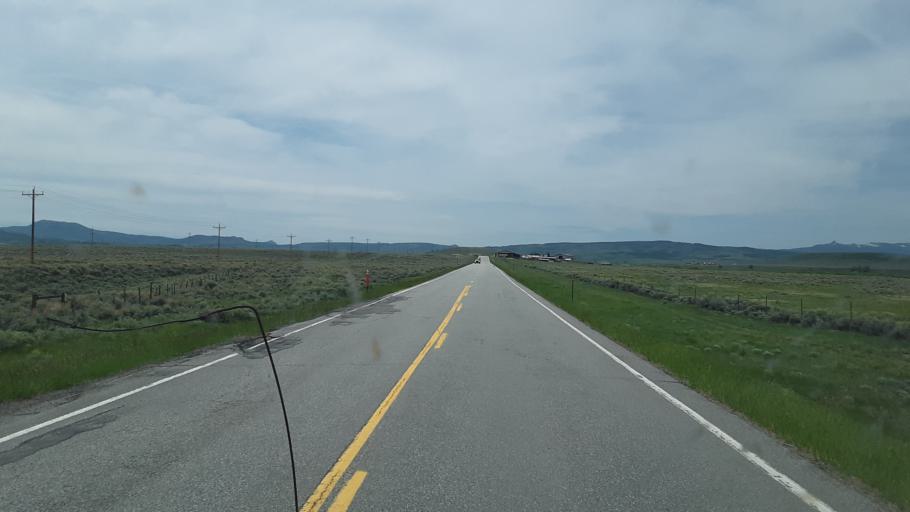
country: US
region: Colorado
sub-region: Jackson County
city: Walden
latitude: 40.5231
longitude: -106.4122
